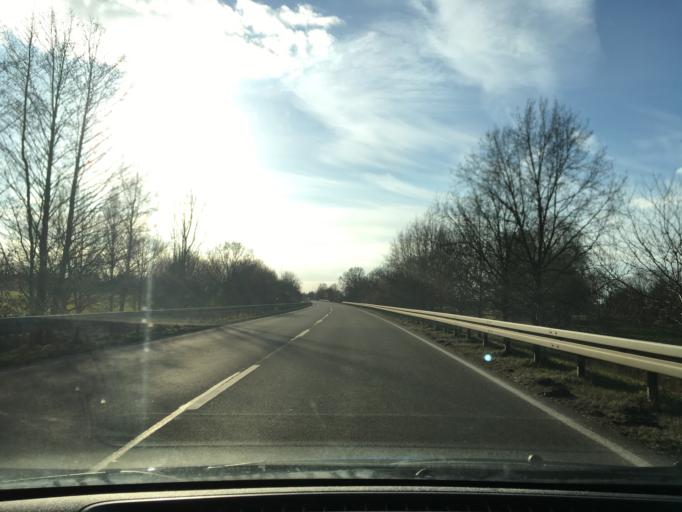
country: DE
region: Saxony-Anhalt
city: Luftkurort Arendsee
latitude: 52.8785
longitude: 11.5130
